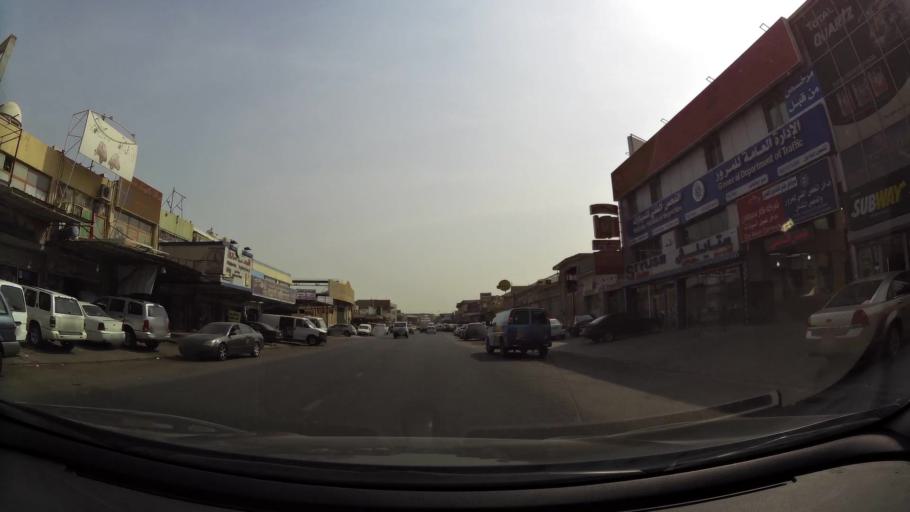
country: KW
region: Al Asimah
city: Ar Rabiyah
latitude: 29.3178
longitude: 47.9328
